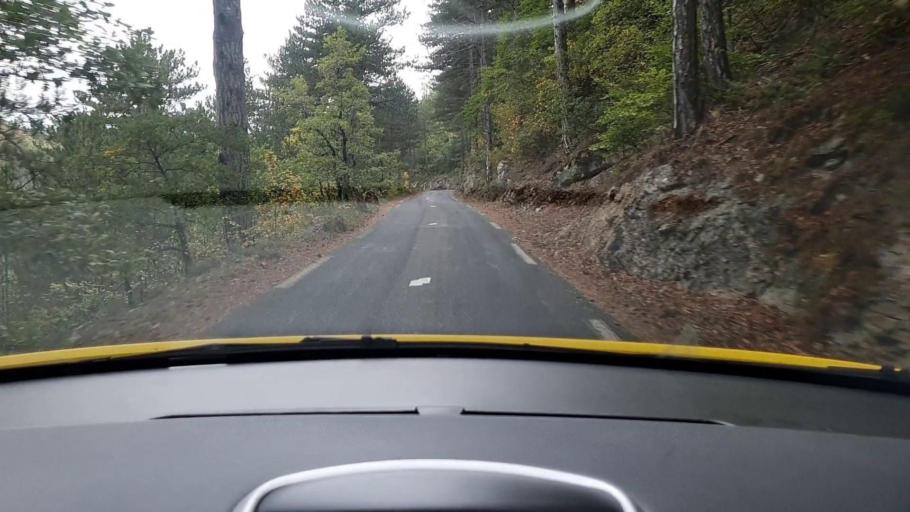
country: FR
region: Languedoc-Roussillon
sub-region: Departement de la Lozere
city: Meyrueis
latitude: 44.0814
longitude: 3.3622
